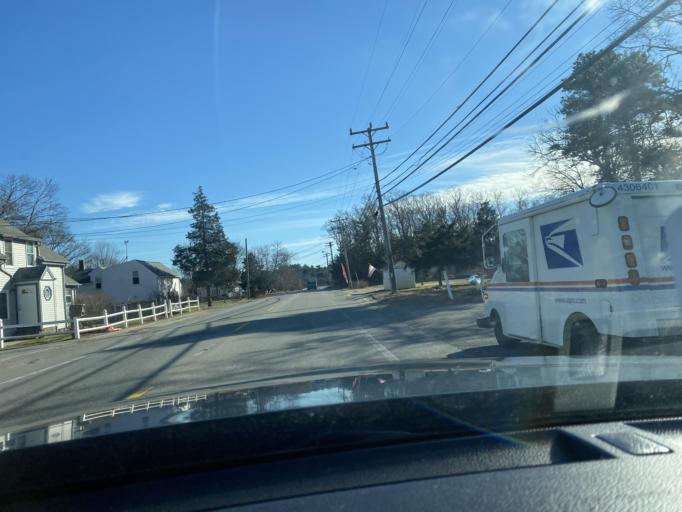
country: US
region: Massachusetts
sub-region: Plymouth County
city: West Wareham
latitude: 41.7952
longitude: -70.7601
